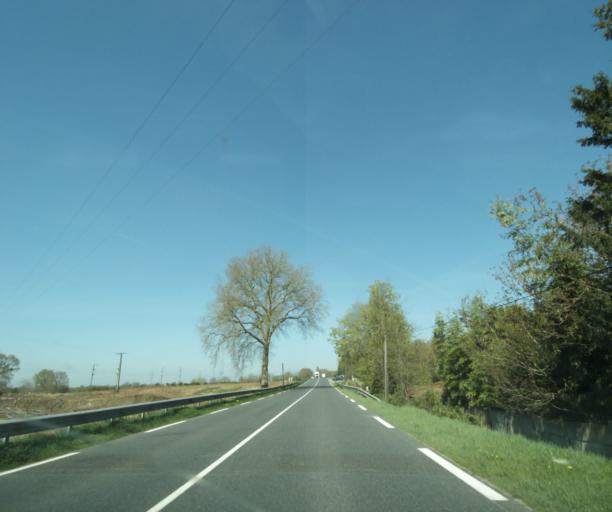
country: FR
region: Bourgogne
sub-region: Departement de la Nievre
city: Chantenay-Saint-Imbert
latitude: 46.6801
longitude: 3.2281
